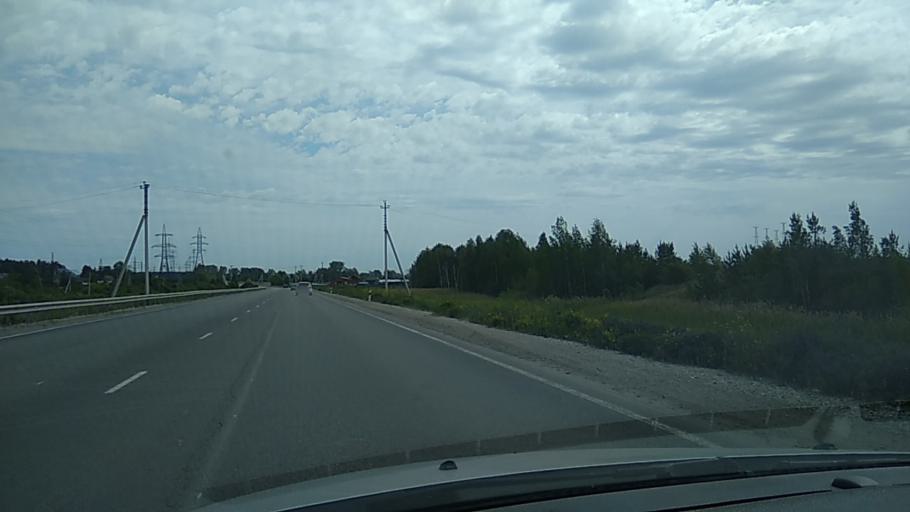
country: RU
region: Sverdlovsk
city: Verkhnyaya Pyshma
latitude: 56.9497
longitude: 60.5929
